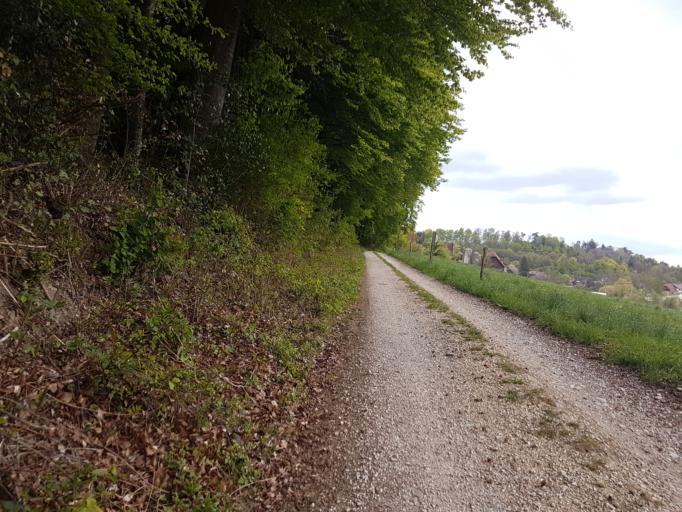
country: CH
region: Bern
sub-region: Seeland District
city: Leuzigen
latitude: 47.1779
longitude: 7.4771
